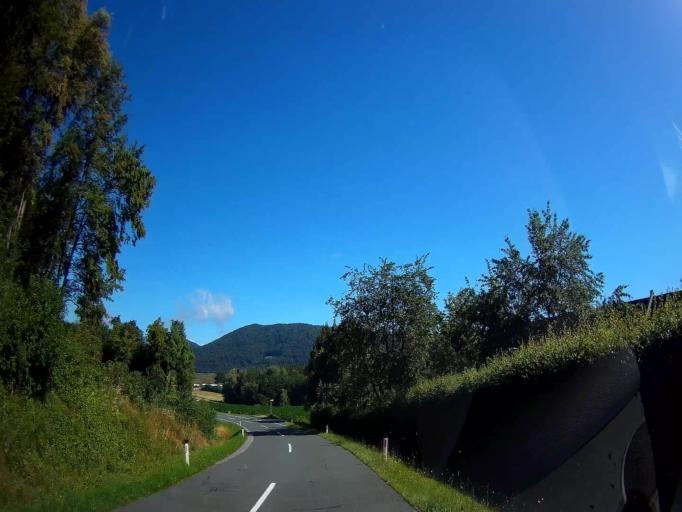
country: AT
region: Carinthia
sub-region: Politischer Bezirk Volkermarkt
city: Voelkermarkt
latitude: 46.6404
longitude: 14.5501
